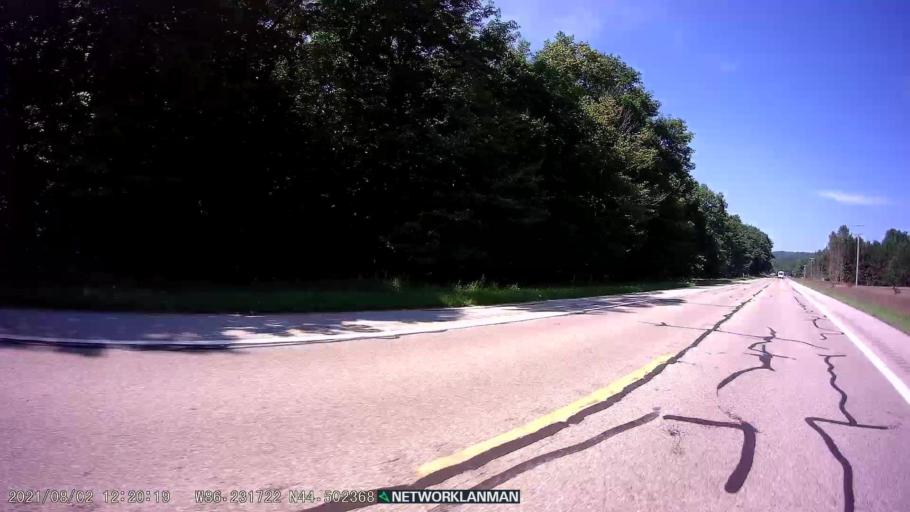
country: US
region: Michigan
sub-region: Benzie County
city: Frankfort
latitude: 44.5025
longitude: -86.2317
